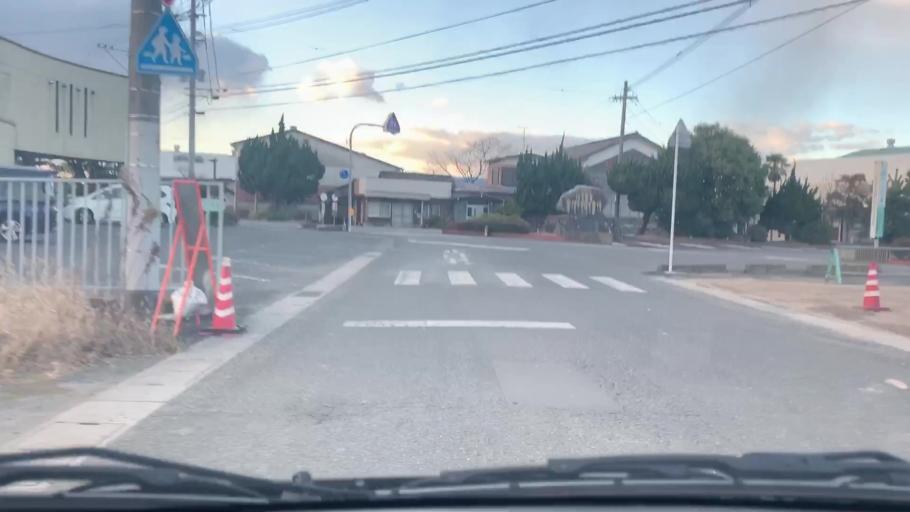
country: JP
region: Saga Prefecture
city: Kashima
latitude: 33.1820
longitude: 130.1887
